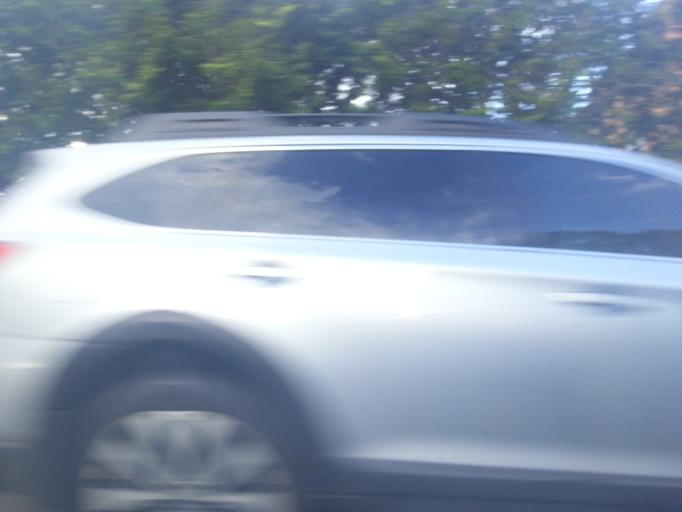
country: AU
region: New South Wales
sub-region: Wollongong
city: West Wollongong
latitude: -34.4244
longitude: 150.8636
